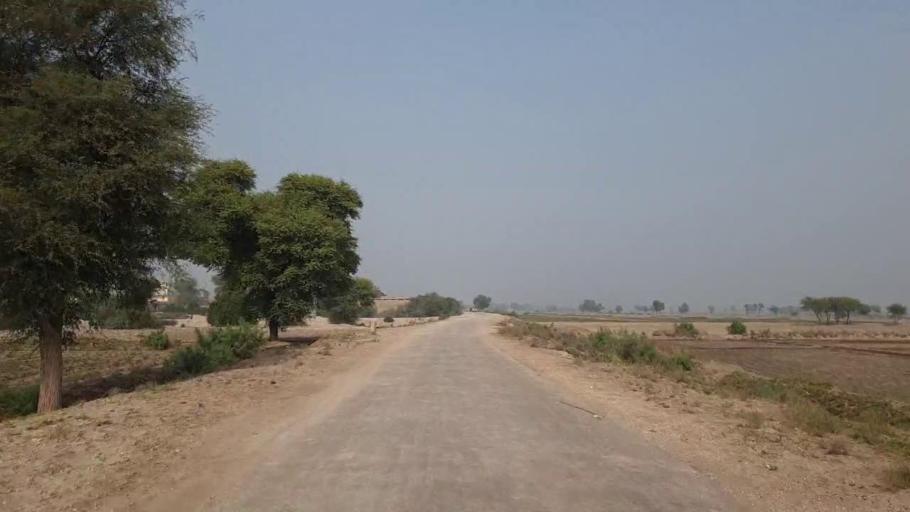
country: PK
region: Sindh
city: Bhan
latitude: 26.5130
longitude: 67.6895
